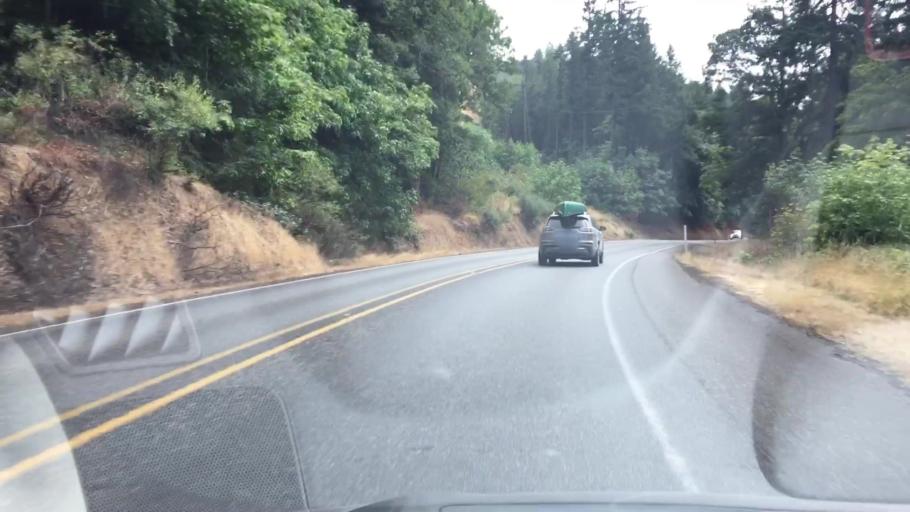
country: US
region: Washington
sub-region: Klickitat County
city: White Salmon
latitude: 45.7517
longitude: -121.5175
